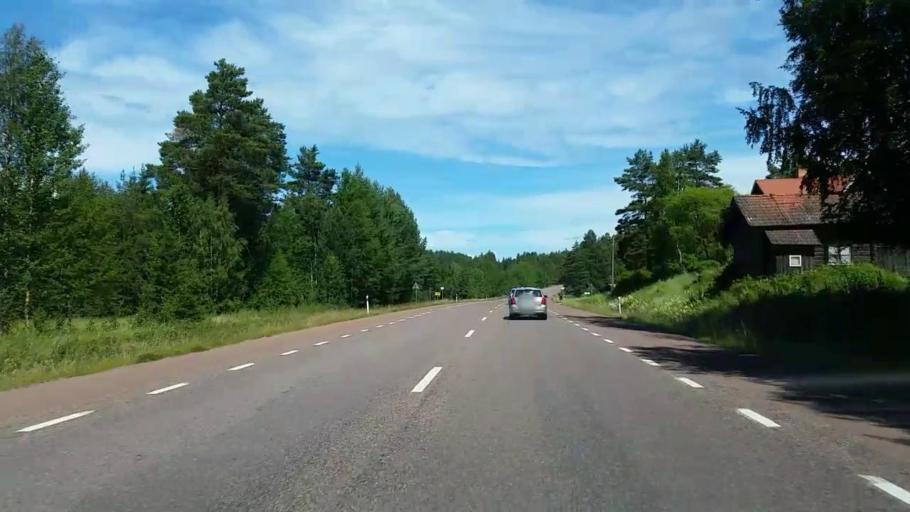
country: SE
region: Dalarna
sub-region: Rattviks Kommun
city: Raettvik
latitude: 60.9202
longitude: 15.2082
